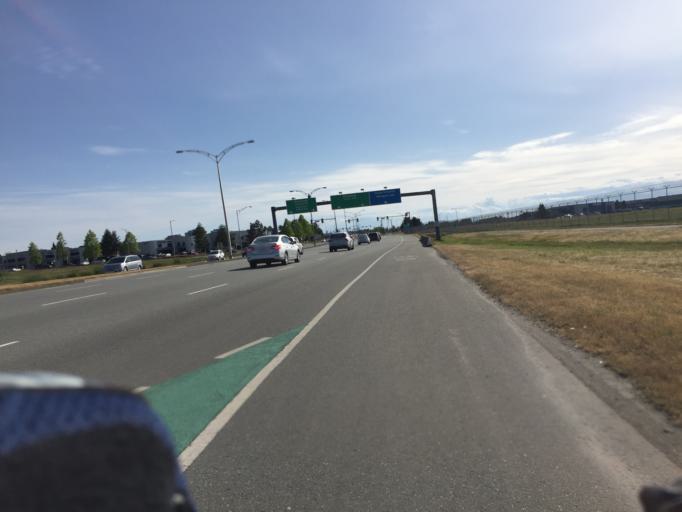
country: CA
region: British Columbia
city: Richmond
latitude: 49.1827
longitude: -123.1498
